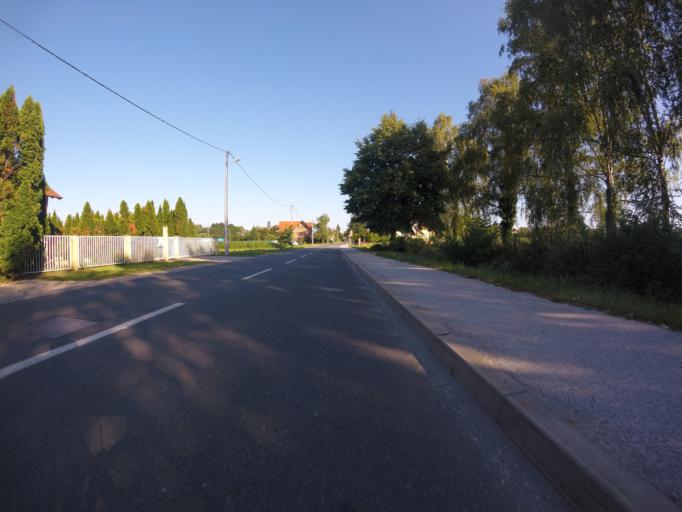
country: HR
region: Grad Zagreb
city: Zadvorsko
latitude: 45.7289
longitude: 15.9050
